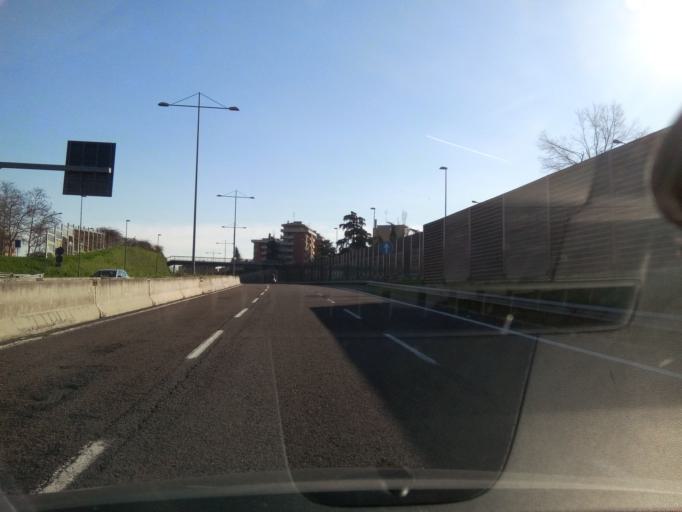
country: IT
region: Emilia-Romagna
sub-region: Provincia di Bologna
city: Casalecchio di Reno
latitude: 44.4924
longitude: 11.2913
